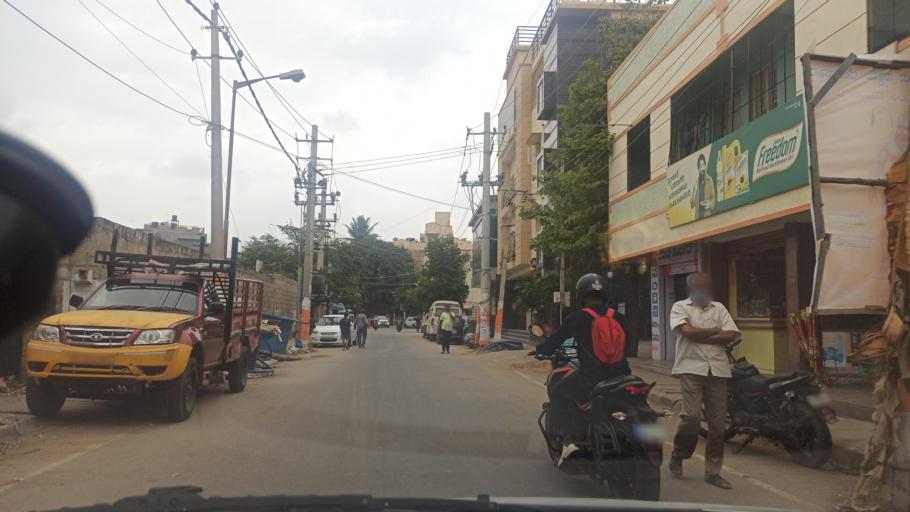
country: IN
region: Karnataka
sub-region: Bangalore Urban
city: Yelahanka
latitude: 13.0397
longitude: 77.6024
